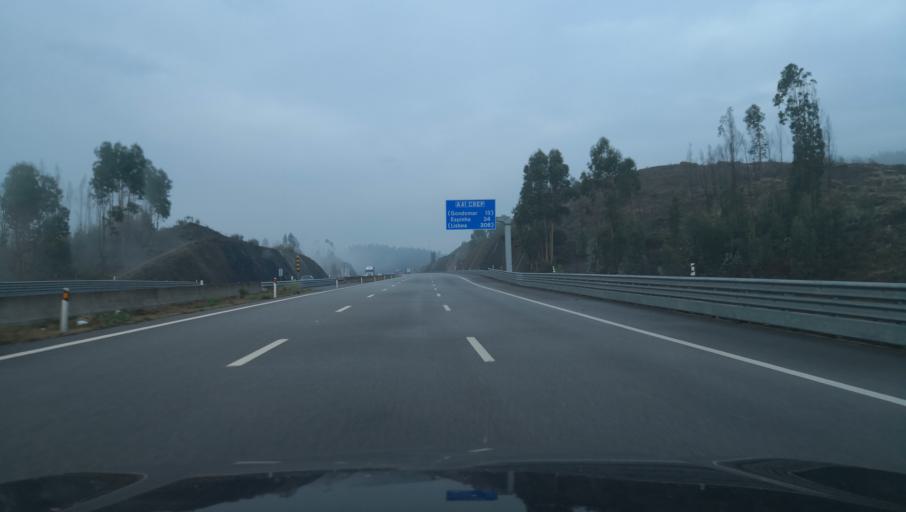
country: PT
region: Porto
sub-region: Paredes
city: Recarei
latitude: 41.1328
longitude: -8.4274
